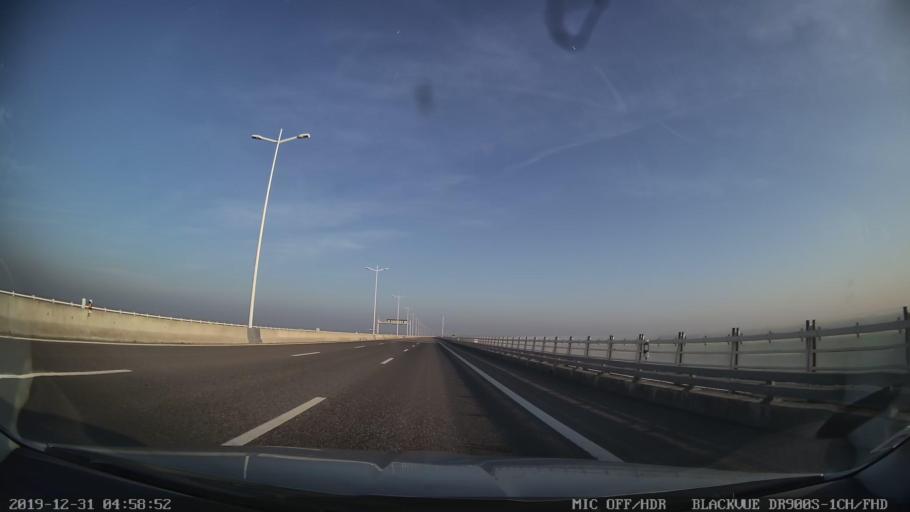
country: PT
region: Lisbon
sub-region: Vila Franca de Xira
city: Castanheira do Ribatejo
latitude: 39.0113
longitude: -8.9306
